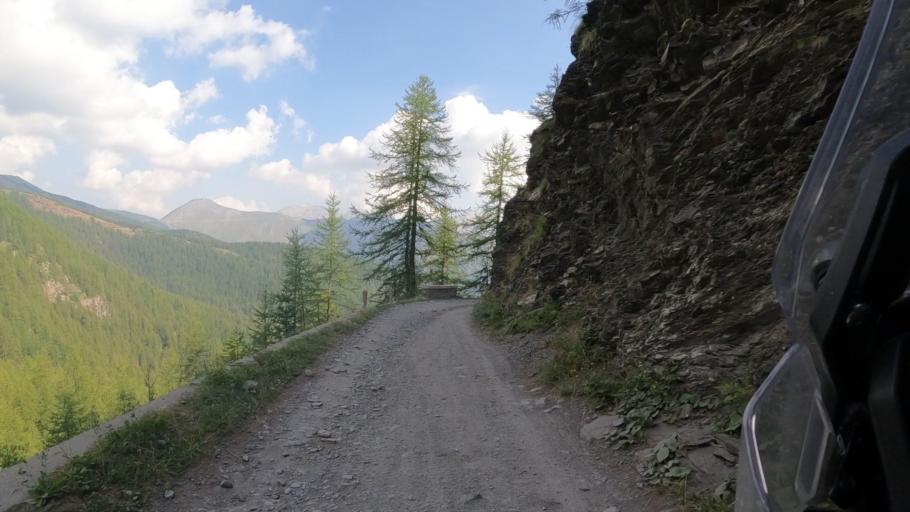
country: IT
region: Piedmont
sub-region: Provincia di Cuneo
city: Briga Alta
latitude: 44.1021
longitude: 7.7167
